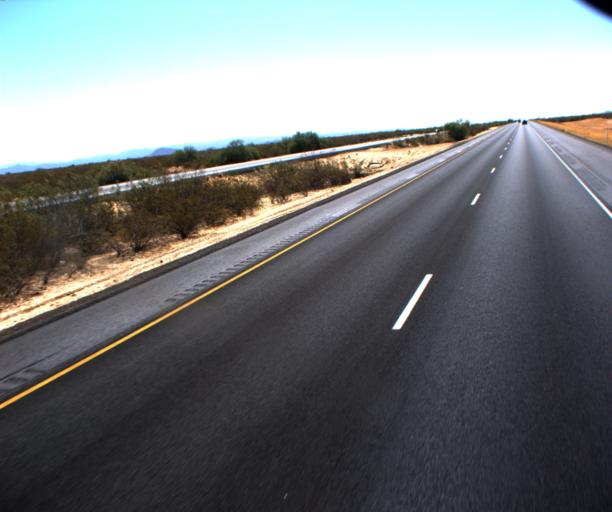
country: US
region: Arizona
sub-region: Yavapai County
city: Congress
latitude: 34.0789
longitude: -112.8872
